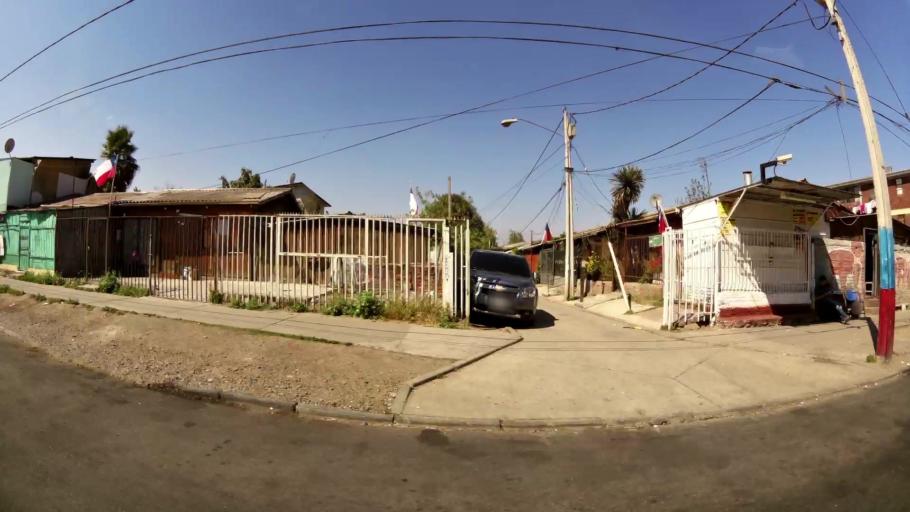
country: CL
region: Santiago Metropolitan
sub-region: Provincia de Santiago
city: Lo Prado
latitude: -33.4088
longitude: -70.7371
